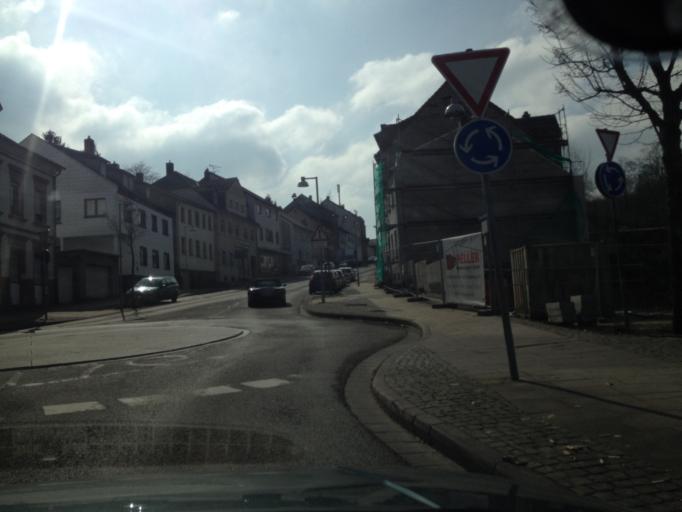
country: DE
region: Saarland
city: Friedrichsthal
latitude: 49.3101
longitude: 7.0813
